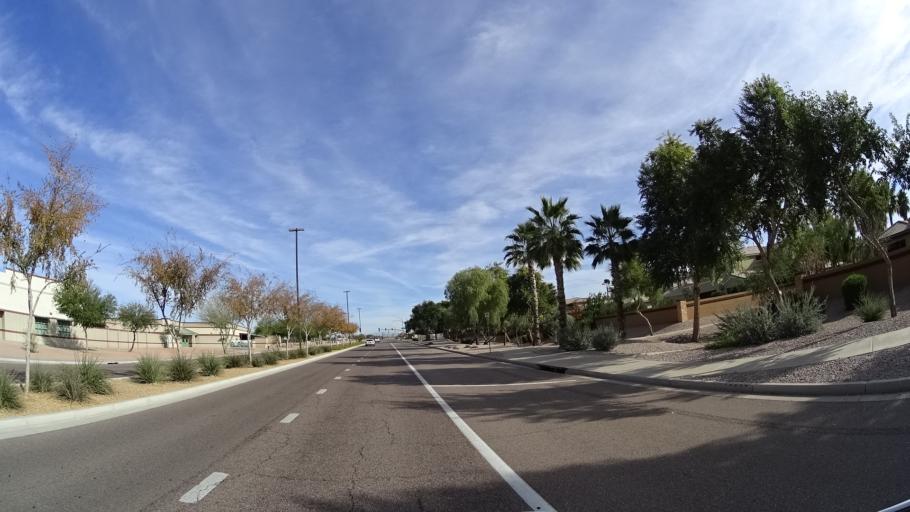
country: US
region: Arizona
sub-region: Maricopa County
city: Gilbert
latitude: 33.2775
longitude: -111.7623
